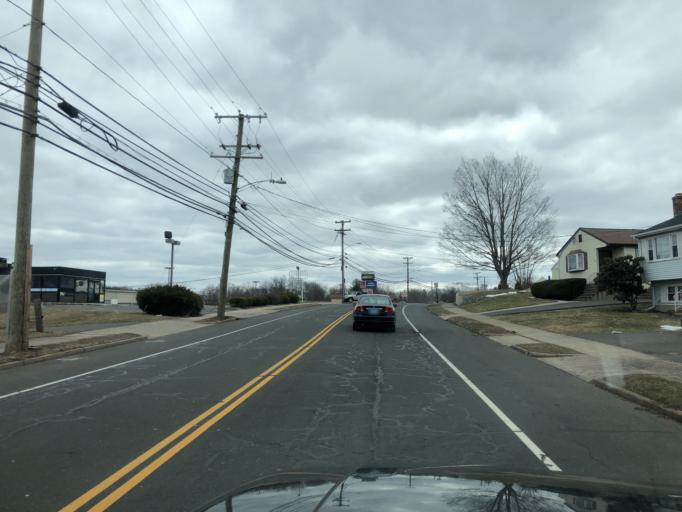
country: US
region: Connecticut
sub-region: Hartford County
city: New Britain
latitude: 41.6979
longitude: -72.7914
